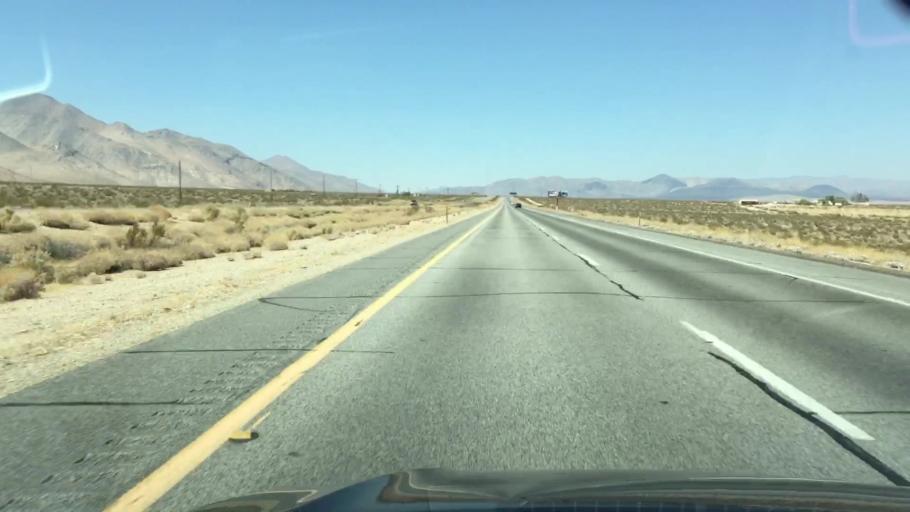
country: US
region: California
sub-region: Kern County
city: Inyokern
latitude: 35.7132
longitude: -117.8682
